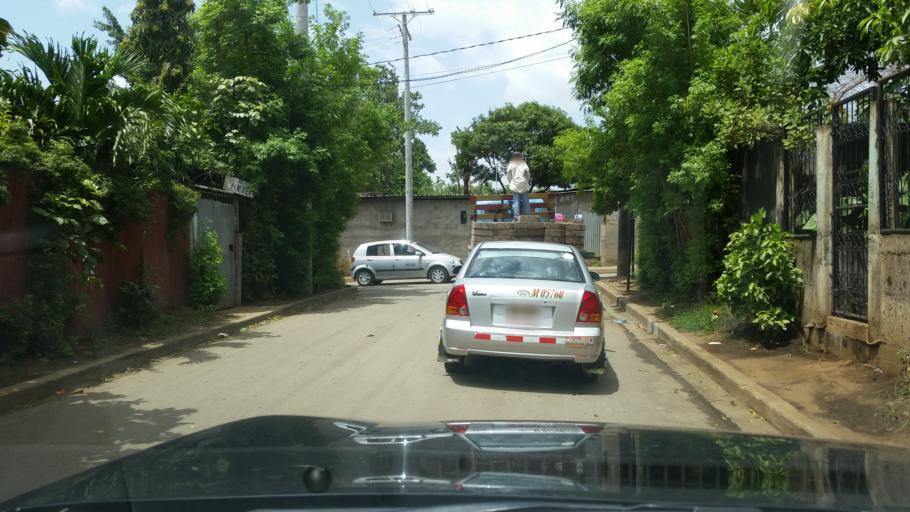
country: NI
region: Managua
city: Managua
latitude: 12.1130
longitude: -86.2171
